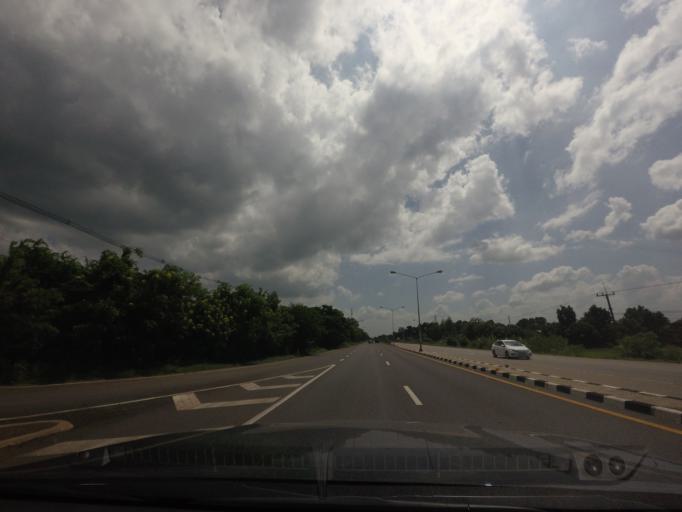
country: TH
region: Phetchabun
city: Nong Phai
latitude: 16.1986
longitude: 101.0890
